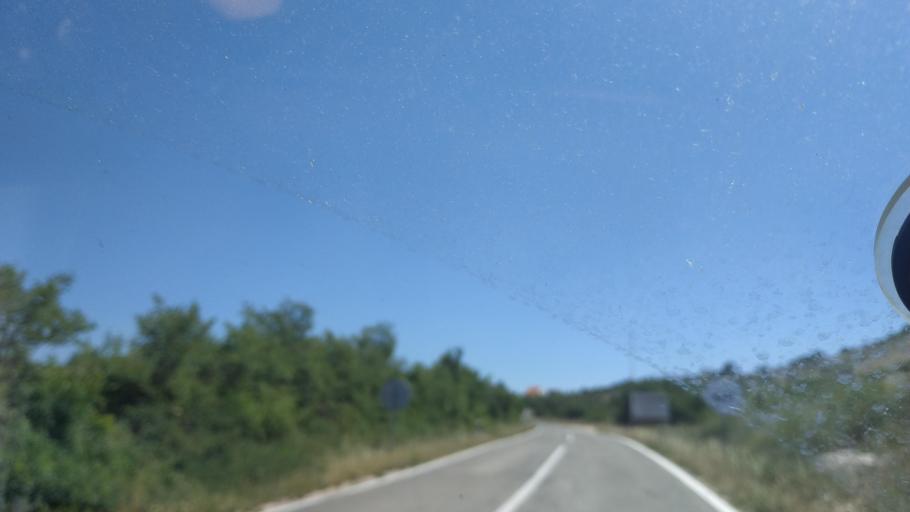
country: HR
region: Sibensko-Kniniska
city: Drnis
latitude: 43.9039
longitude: 16.2088
